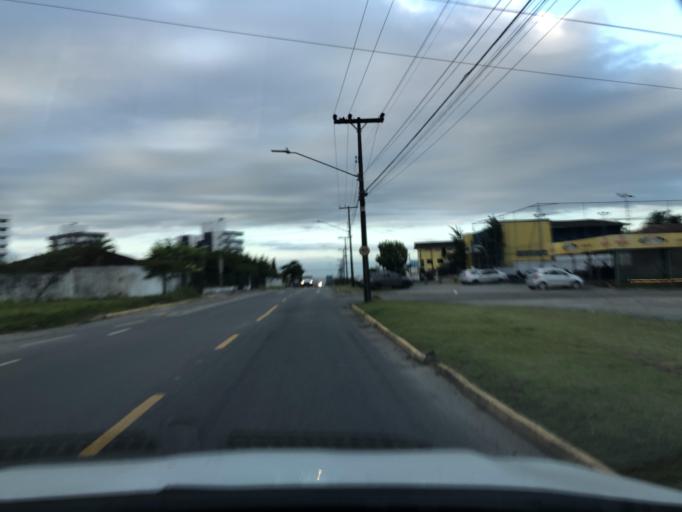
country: BR
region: Santa Catarina
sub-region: Joinville
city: Joinville
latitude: -26.2738
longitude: -48.8633
